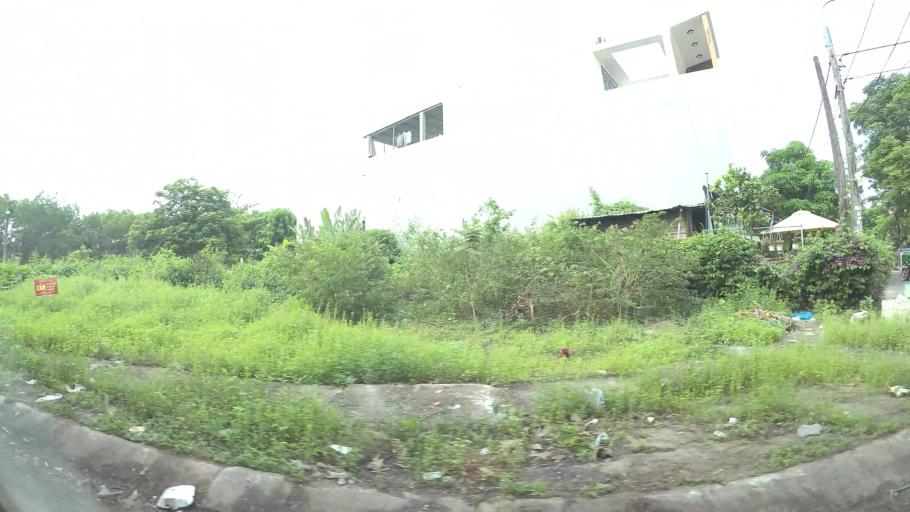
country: VN
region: Da Nang
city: Lien Chieu
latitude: 16.0578
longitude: 108.1616
